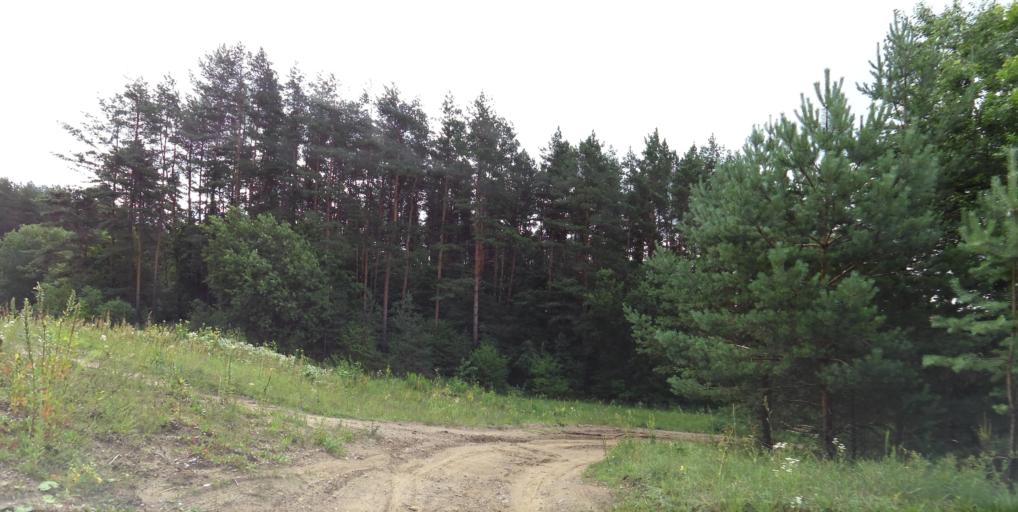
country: LT
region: Vilnius County
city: Pilaite
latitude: 54.6994
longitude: 25.1950
